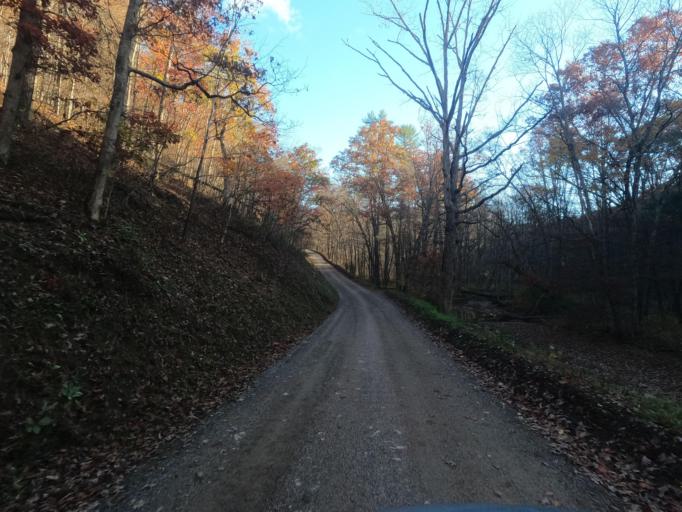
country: US
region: West Virginia
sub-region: Morgan County
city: Berkeley Springs
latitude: 39.6604
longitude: -78.4622
